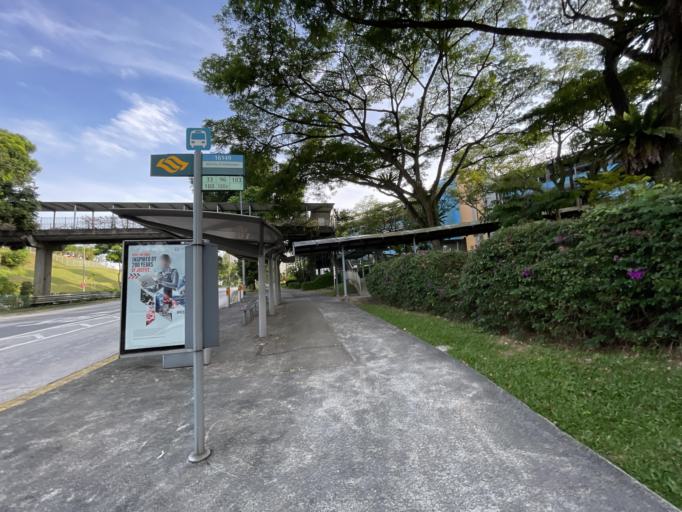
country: SG
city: Singapore
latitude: 1.2977
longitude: 103.7699
